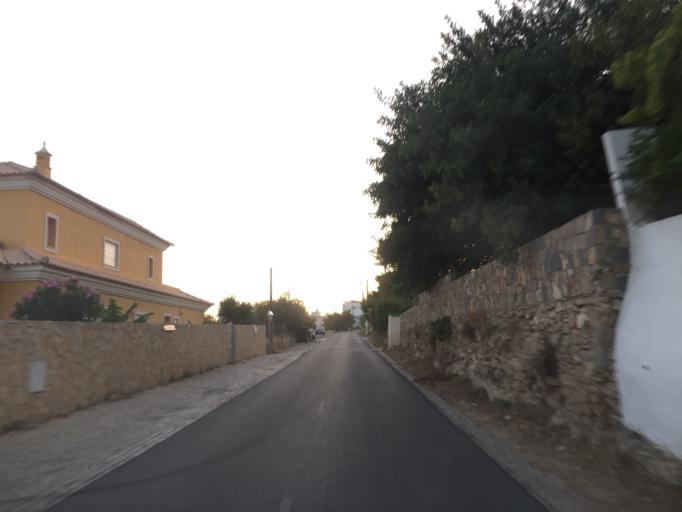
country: PT
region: Faro
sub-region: Faro
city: Santa Barbara de Nexe
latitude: 37.1045
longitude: -7.9954
